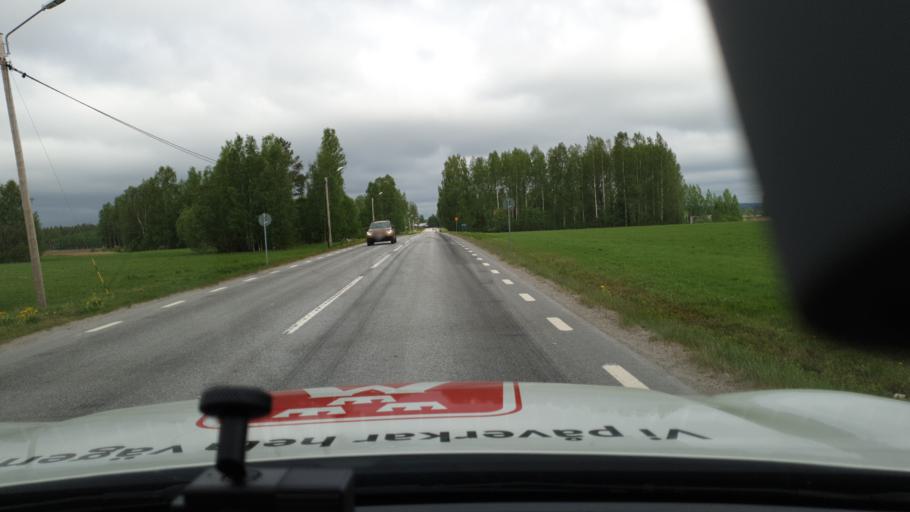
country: SE
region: Vaesterbotten
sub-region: Umea Kommun
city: Roback
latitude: 63.9285
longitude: 20.1800
